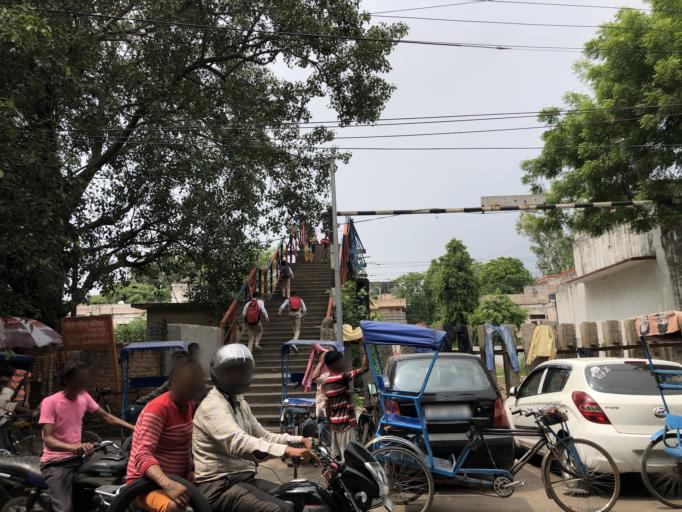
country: IN
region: NCT
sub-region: New Delhi
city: New Delhi
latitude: 28.5787
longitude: 77.2414
